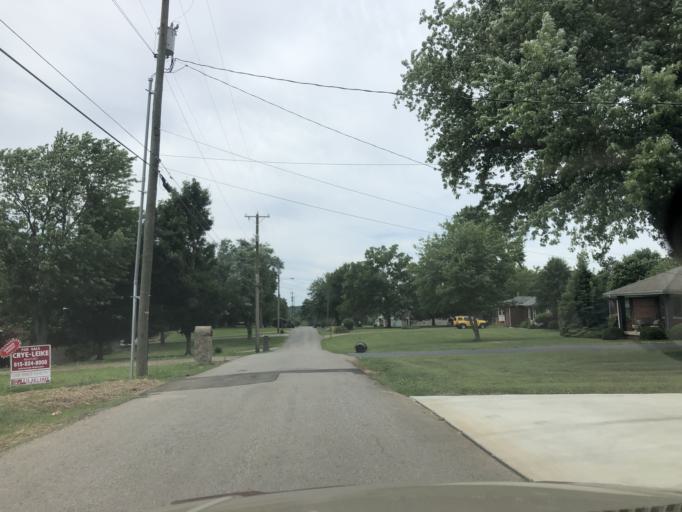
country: US
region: Tennessee
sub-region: Davidson County
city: Lakewood
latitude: 36.2544
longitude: -86.6170
